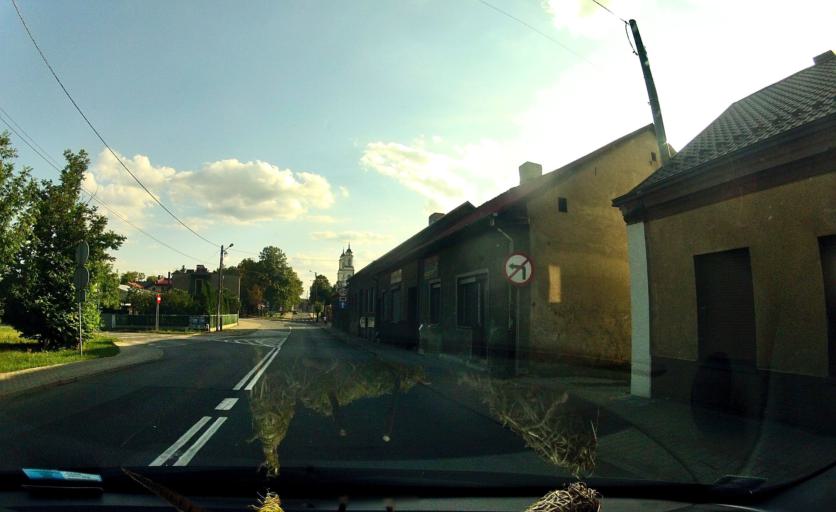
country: PL
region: Opole Voivodeship
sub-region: Powiat oleski
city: Praszka
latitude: 51.0587
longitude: 18.4510
